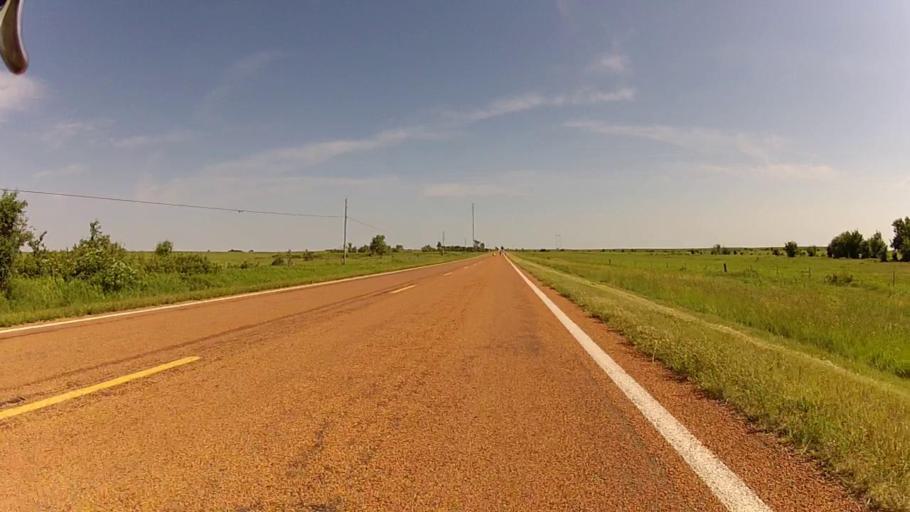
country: US
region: Kansas
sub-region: Cowley County
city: Winfield
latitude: 37.1039
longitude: -96.6436
